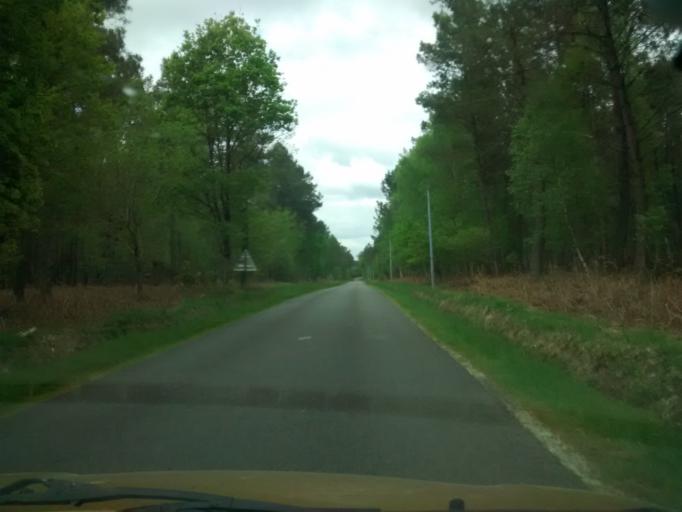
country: FR
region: Brittany
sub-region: Departement du Morbihan
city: Molac
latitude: 47.7377
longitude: -2.4197
